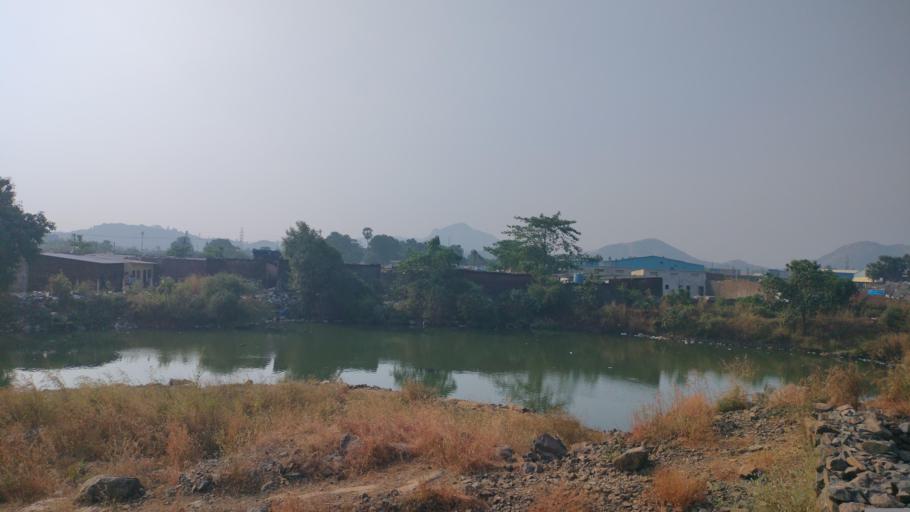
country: IN
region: Maharashtra
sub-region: Thane
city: Virar
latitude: 19.4345
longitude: 72.8852
